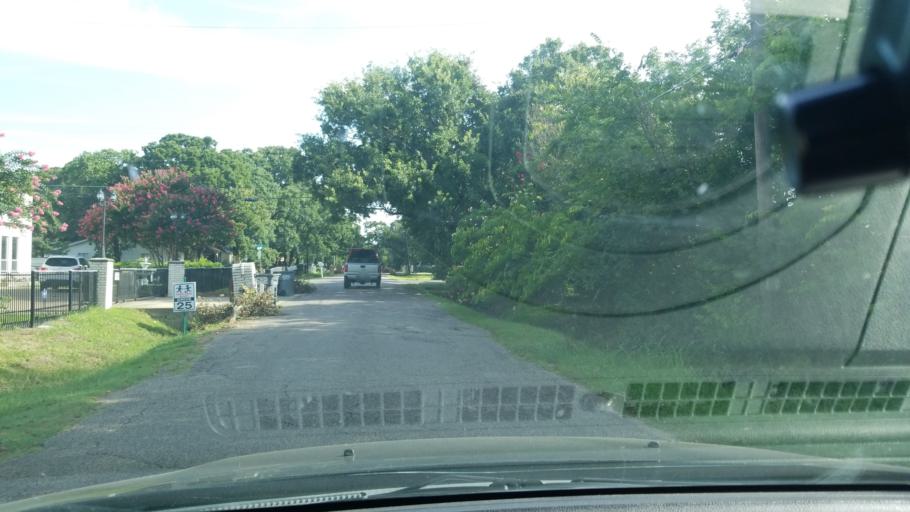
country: US
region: Texas
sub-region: Dallas County
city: Balch Springs
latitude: 32.7153
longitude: -96.6330
